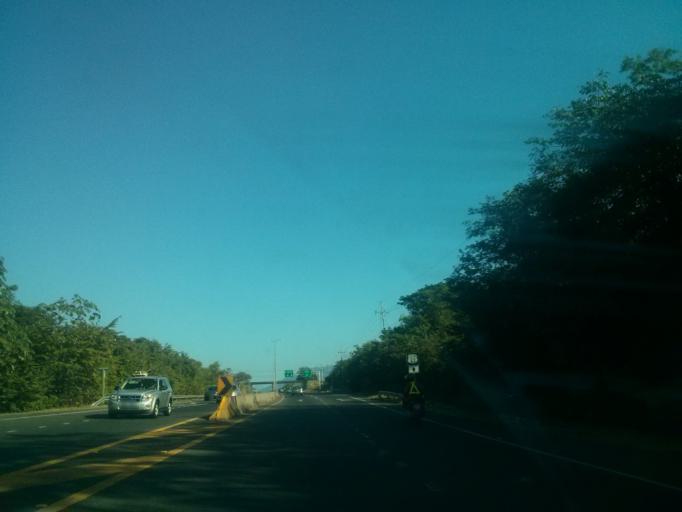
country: CR
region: Alajuela
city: Orotina
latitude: 9.8931
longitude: -84.6155
